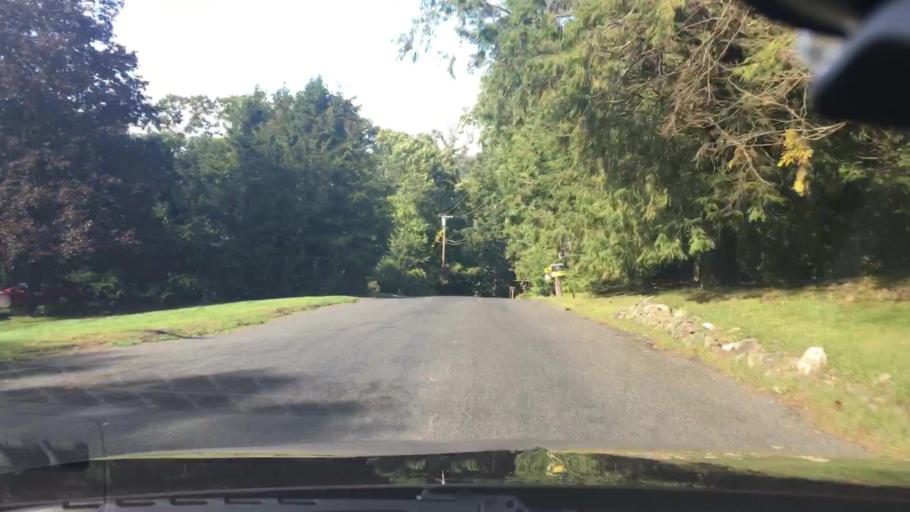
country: US
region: Connecticut
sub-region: Tolland County
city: Somers
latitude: 41.9731
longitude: -72.4135
